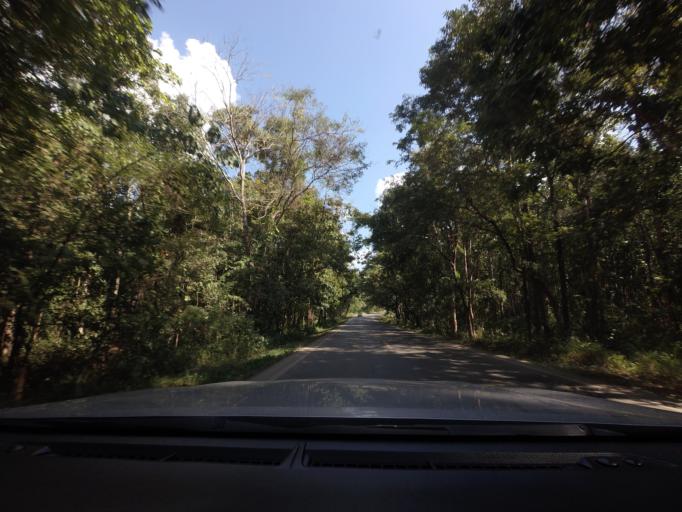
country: TH
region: Chiang Mai
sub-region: Amphoe Chiang Dao
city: Chiang Dao
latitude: 19.4973
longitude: 99.0397
